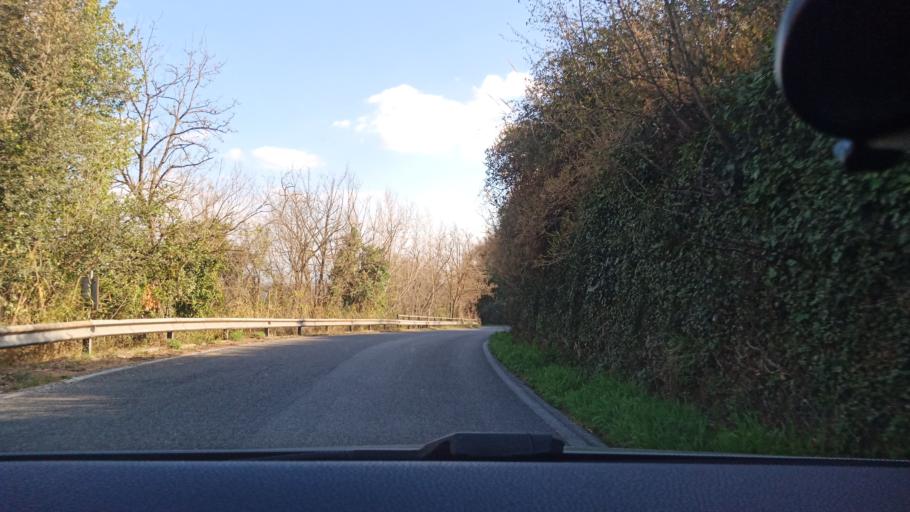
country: IT
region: Latium
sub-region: Citta metropolitana di Roma Capitale
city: Torrita Tiberina
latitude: 42.2471
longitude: 12.6188
